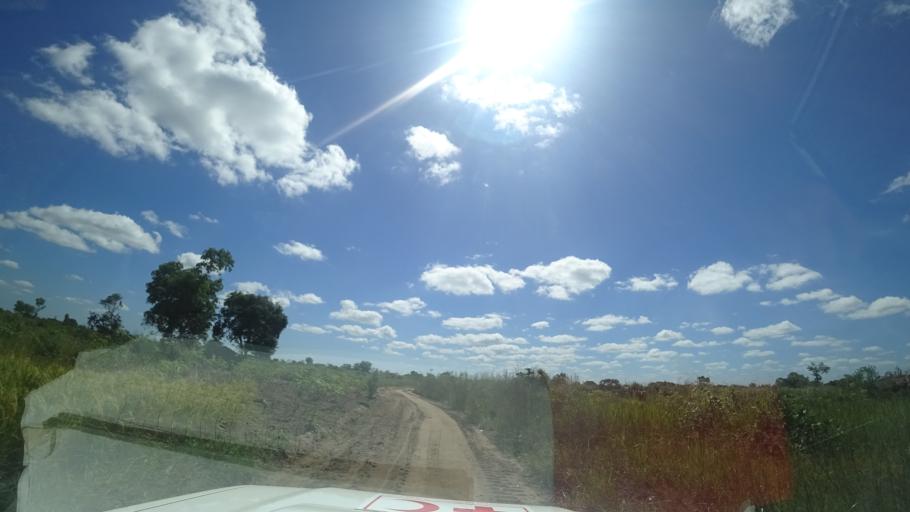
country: MZ
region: Sofala
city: Dondo
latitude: -19.4579
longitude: 34.5941
